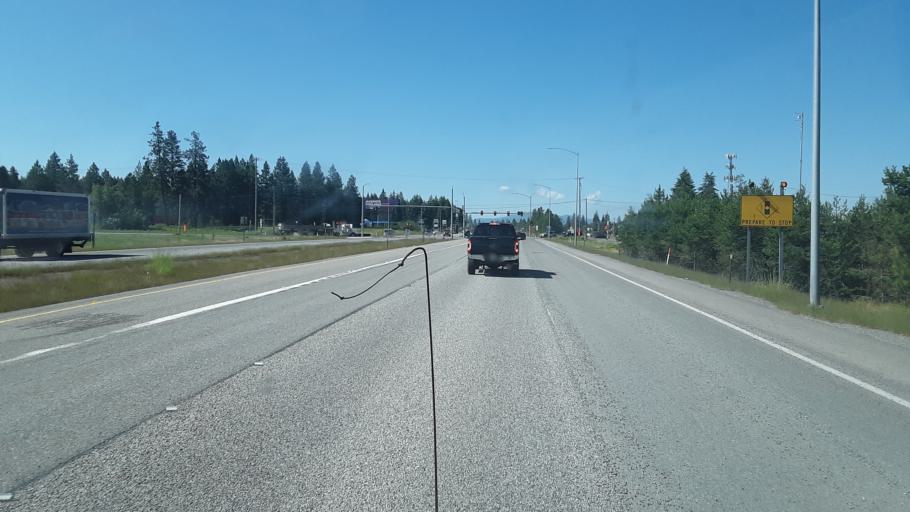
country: US
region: Idaho
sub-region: Kootenai County
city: Hayden
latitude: 47.8334
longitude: -116.7765
